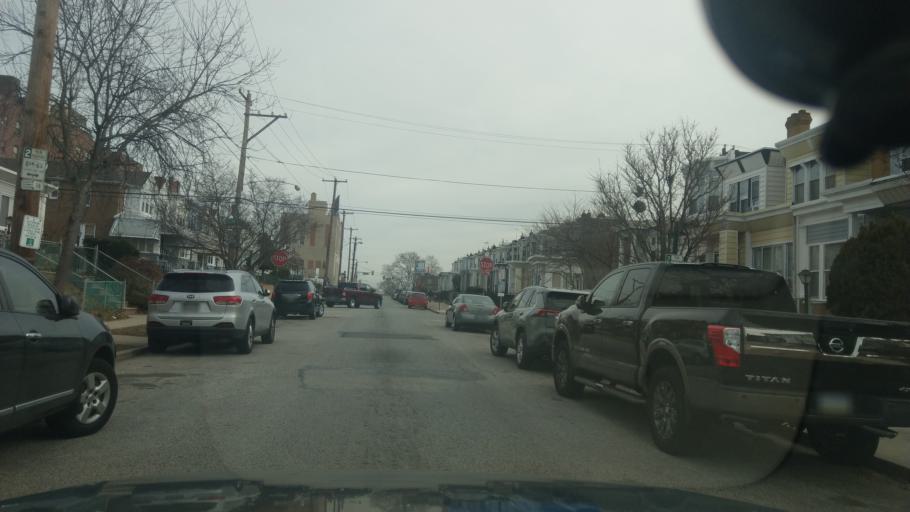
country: US
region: Pennsylvania
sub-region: Montgomery County
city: Wyncote
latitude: 40.0402
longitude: -75.1470
